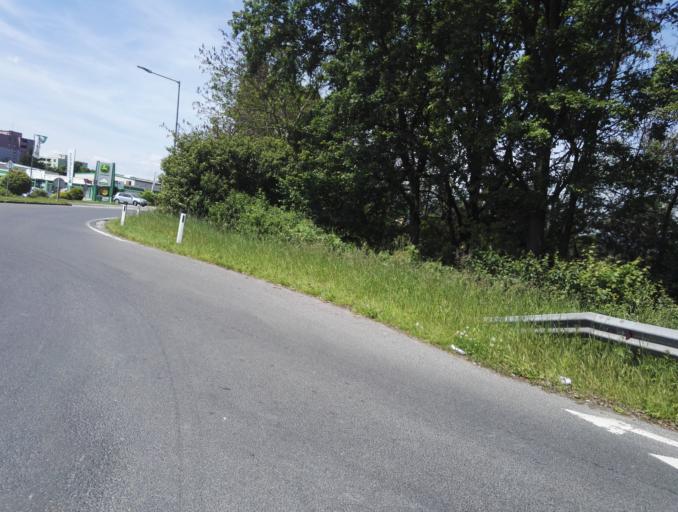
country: AT
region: Styria
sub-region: Politischer Bezirk Graz-Umgebung
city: Kalsdorf bei Graz
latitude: 46.9730
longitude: 15.4723
